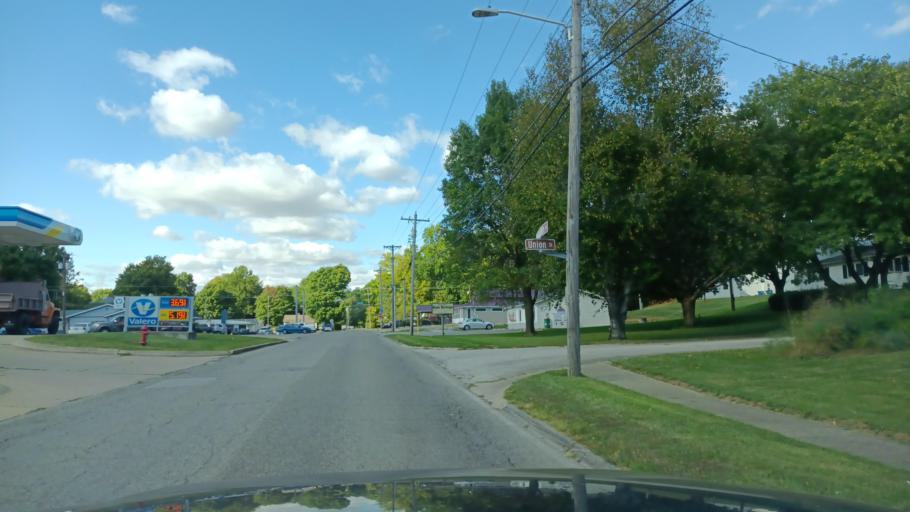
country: US
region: Indiana
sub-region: Fountain County
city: Covington
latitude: 40.1369
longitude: -87.3866
